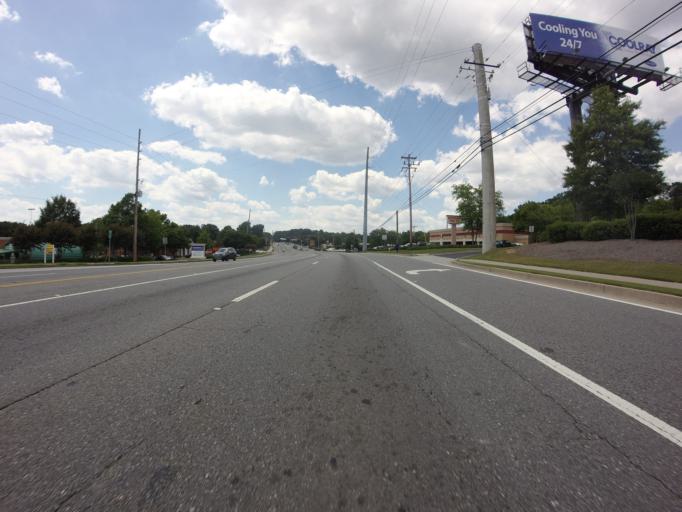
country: US
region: Georgia
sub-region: DeKalb County
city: Dunwoody
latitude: 33.9880
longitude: -84.2727
